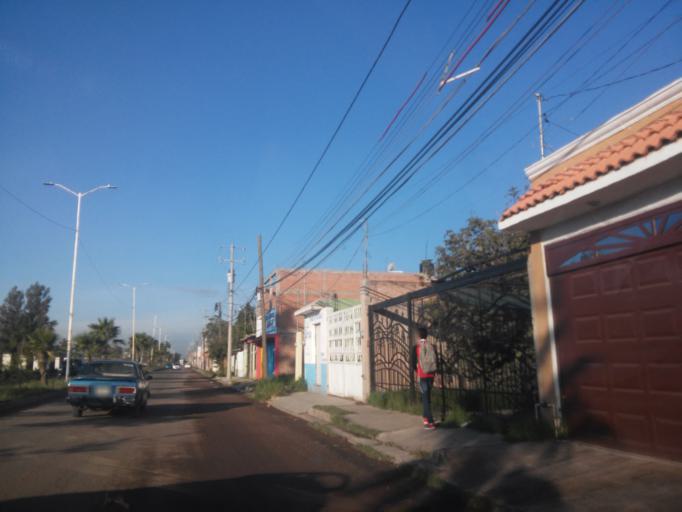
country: MX
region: Durango
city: Victoria de Durango
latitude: 24.0498
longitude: -104.6116
